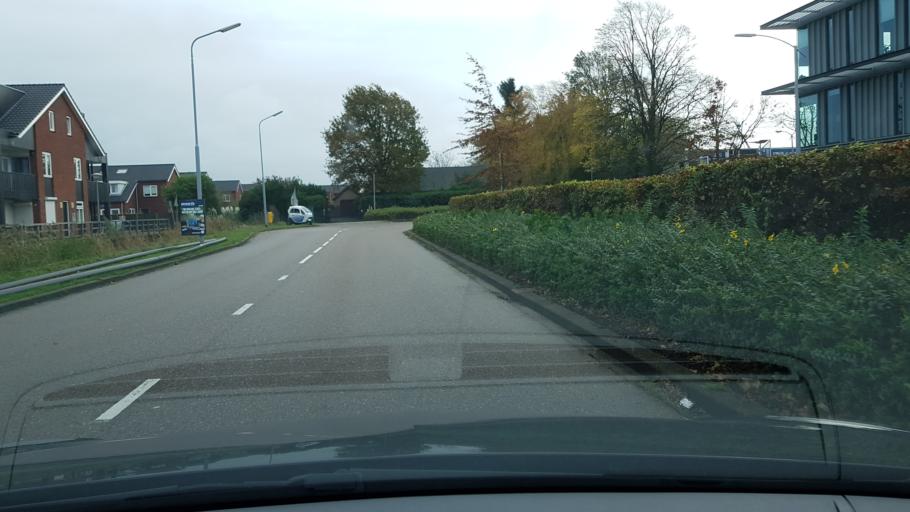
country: NL
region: North Holland
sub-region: Gemeente Heemstede
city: Heemstede
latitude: 52.3358
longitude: 4.6323
